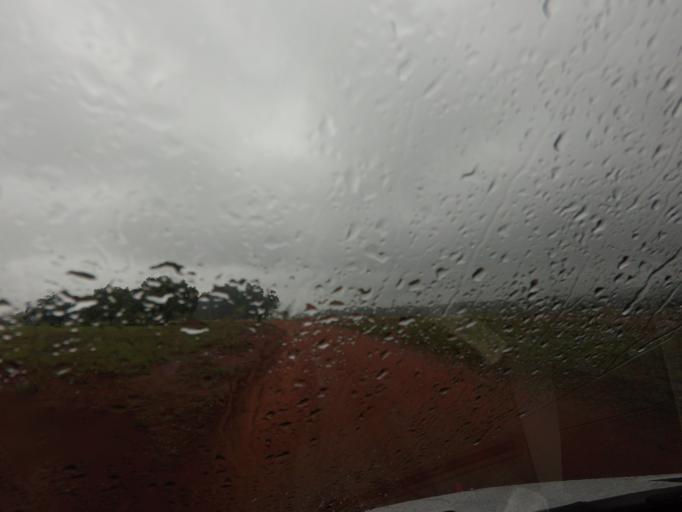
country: SZ
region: Hhohho
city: Lobamba
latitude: -26.4861
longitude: 31.1840
